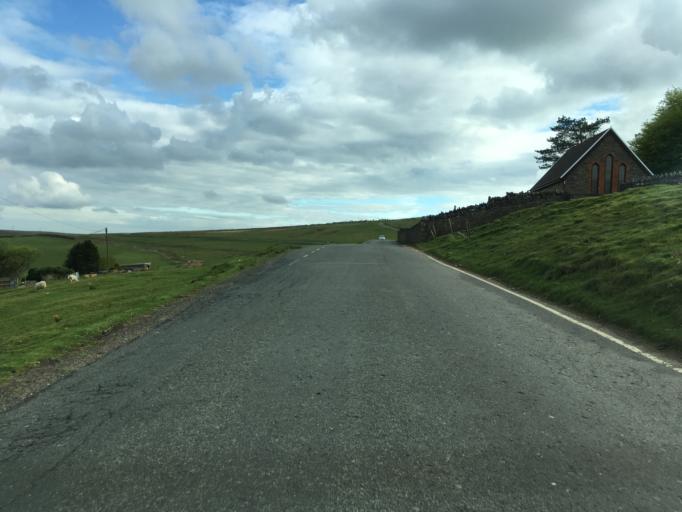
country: GB
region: Wales
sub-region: Caerphilly County Borough
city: Rhymney
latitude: 51.7323
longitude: -3.2993
